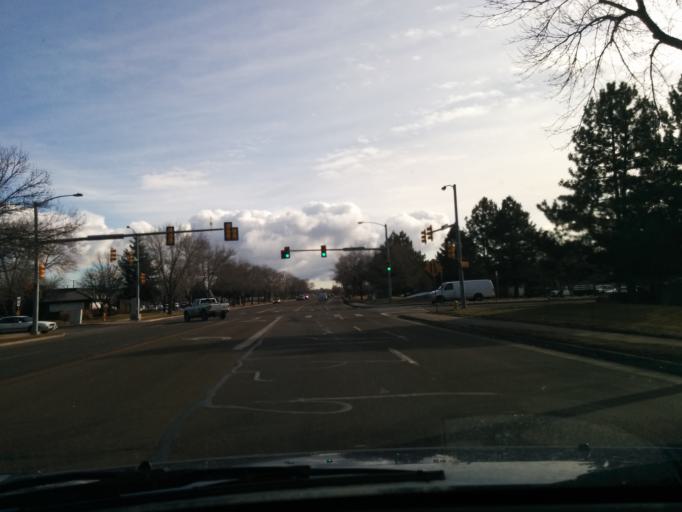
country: US
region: Colorado
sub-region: Larimer County
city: Fort Collins
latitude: 40.5673
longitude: -105.0342
